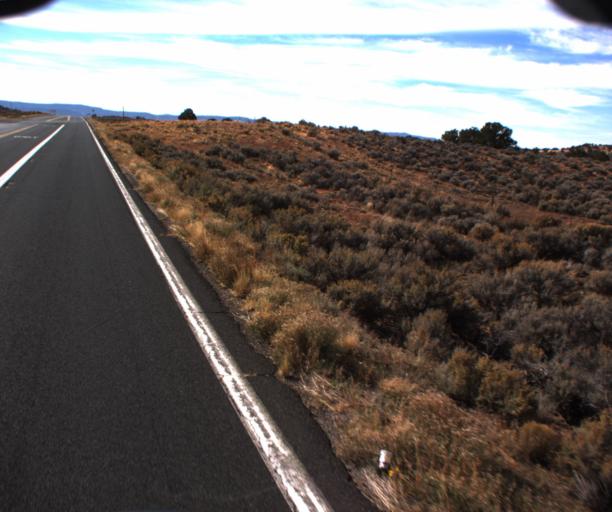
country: US
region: Arizona
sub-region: Coconino County
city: Kaibito
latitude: 36.5473
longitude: -110.7009
